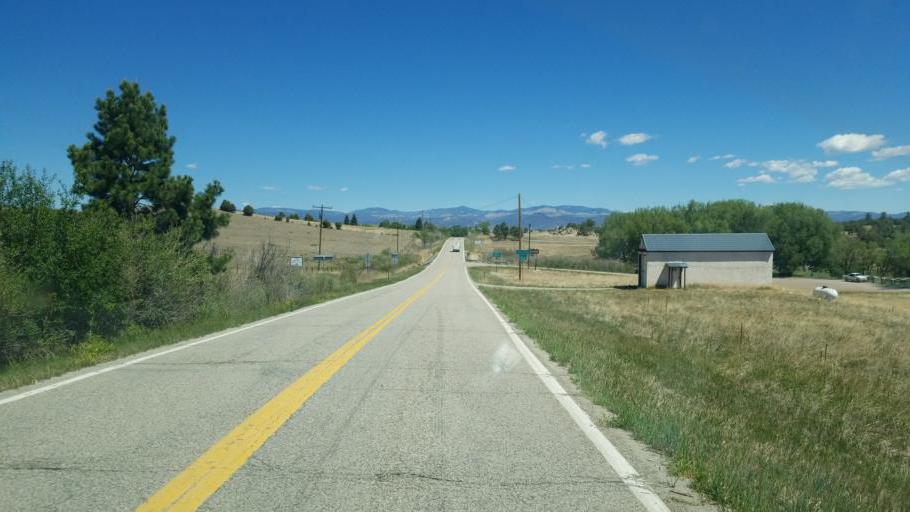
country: US
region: Colorado
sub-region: Custer County
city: Westcliffe
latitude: 38.2644
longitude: -105.6124
